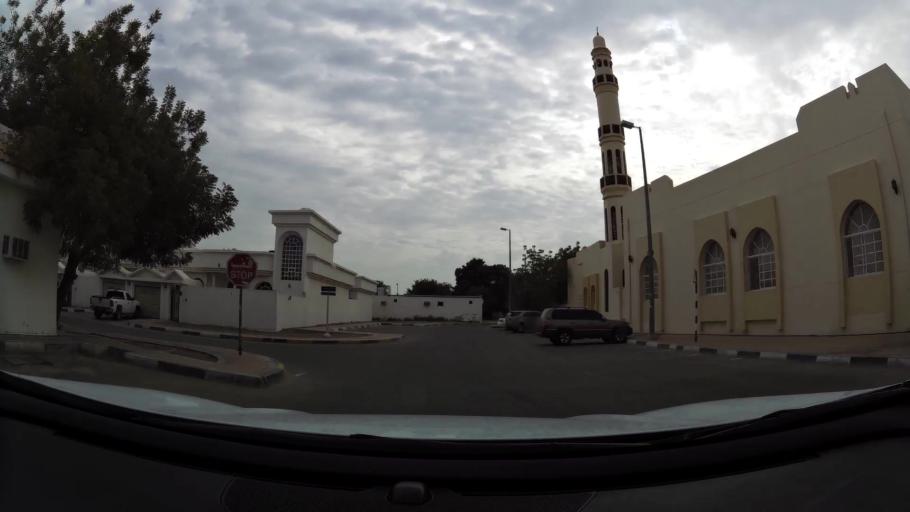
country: AE
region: Abu Dhabi
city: Al Ain
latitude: 24.2235
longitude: 55.7352
